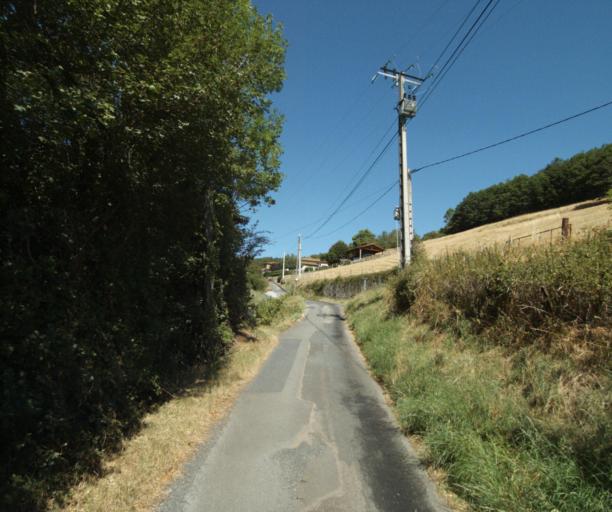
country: FR
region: Rhone-Alpes
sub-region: Departement du Rhone
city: Montrottier
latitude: 45.8033
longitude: 4.5033
